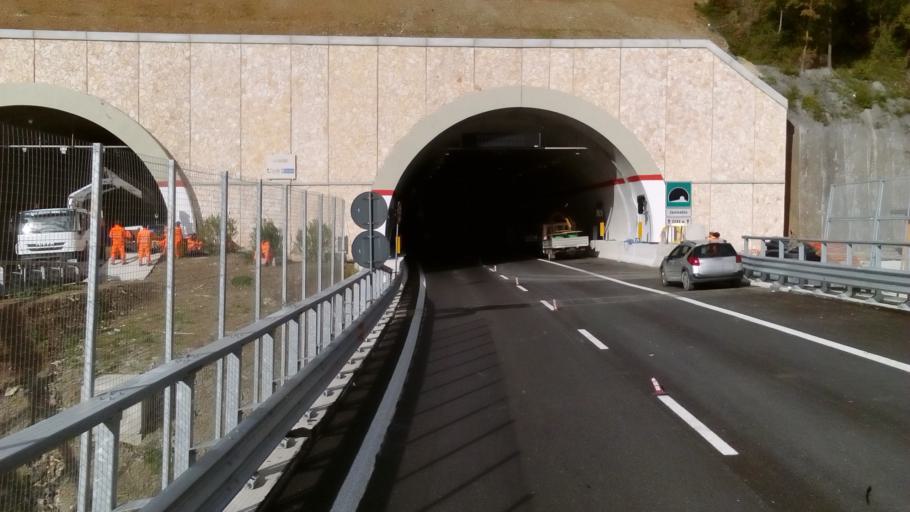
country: IT
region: Calabria
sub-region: Provincia di Cosenza
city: Laino Borgo
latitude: 39.9430
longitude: 15.9593
